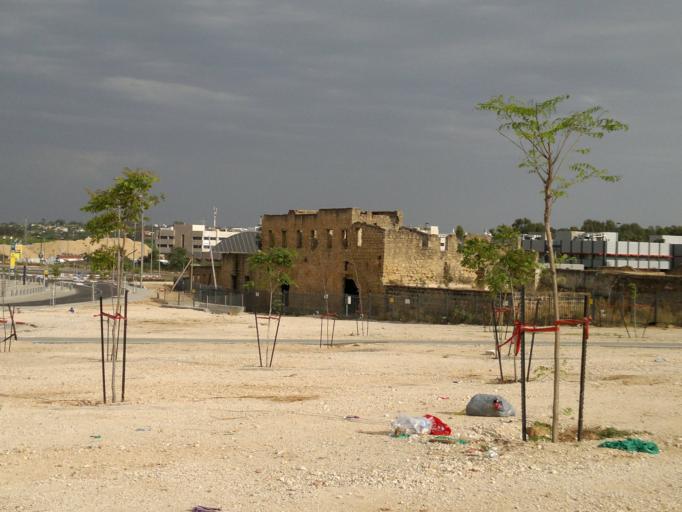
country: IL
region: Central District
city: Even Yehuda
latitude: 32.2945
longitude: 34.8626
